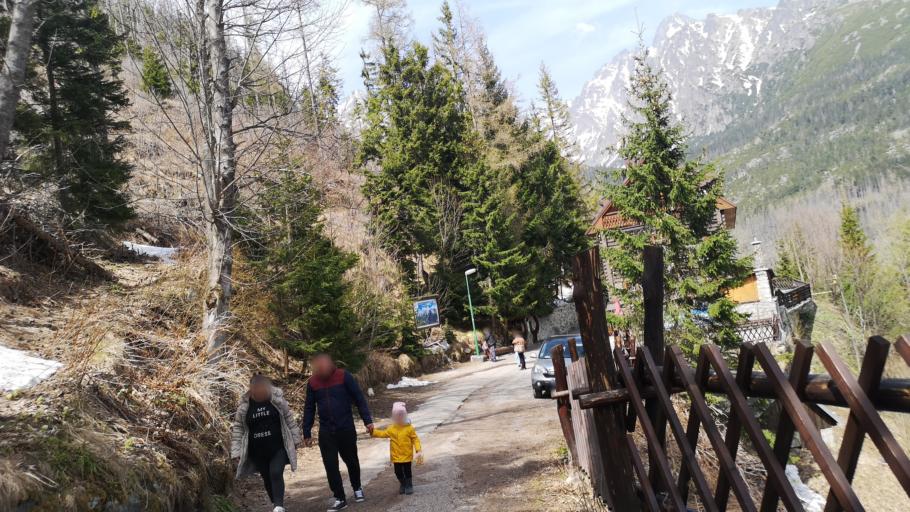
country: SK
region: Presovsky
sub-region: Okres Poprad
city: Vysoke Tatry
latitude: 49.1595
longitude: 20.2246
